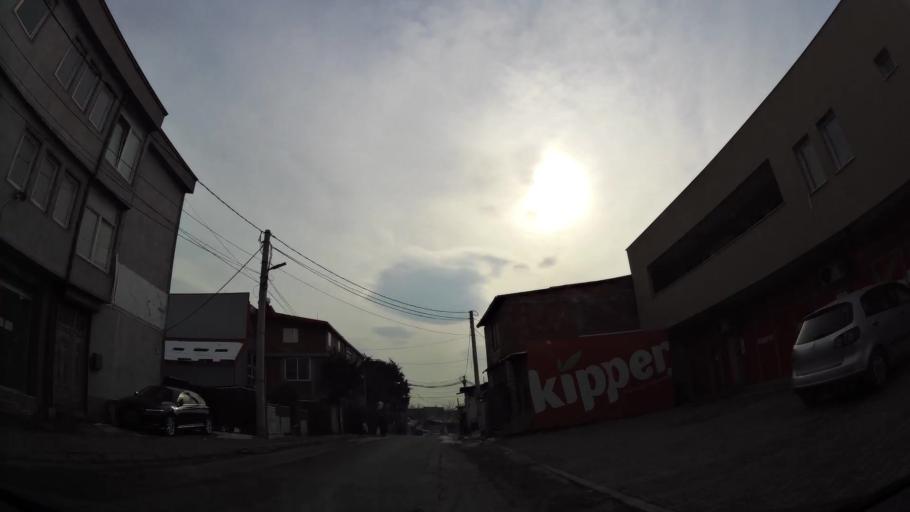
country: MK
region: Cair
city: Cair
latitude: 42.0103
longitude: 21.4334
